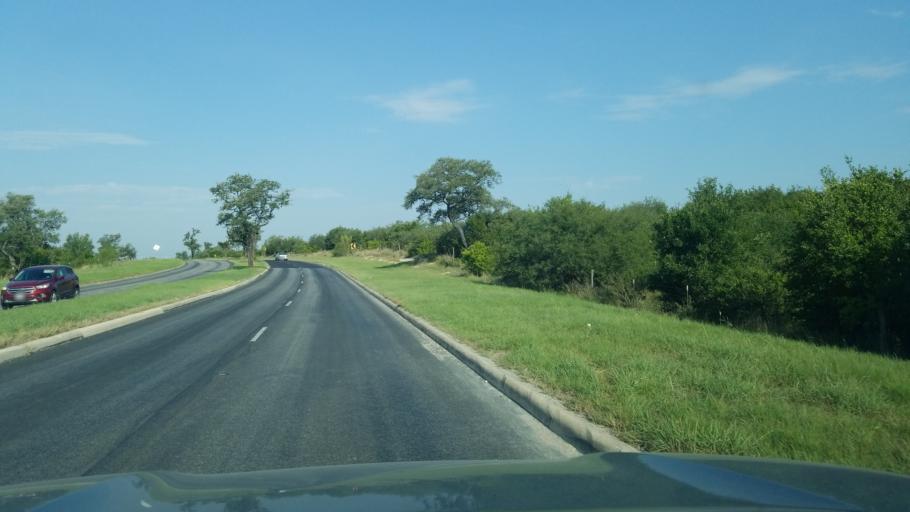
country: US
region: Texas
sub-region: Bexar County
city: Helotes
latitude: 29.4628
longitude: -98.7537
